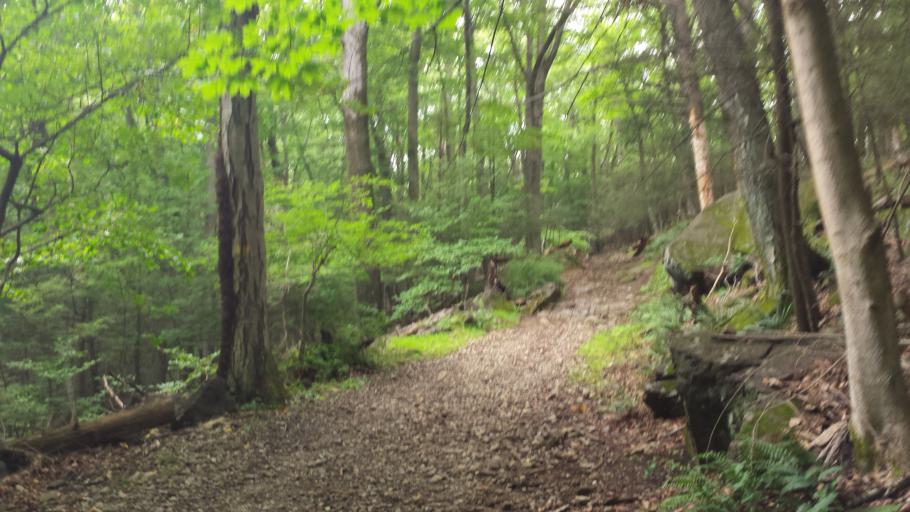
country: US
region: New York
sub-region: Westchester County
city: Peekskill
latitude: 41.2737
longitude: -73.9189
